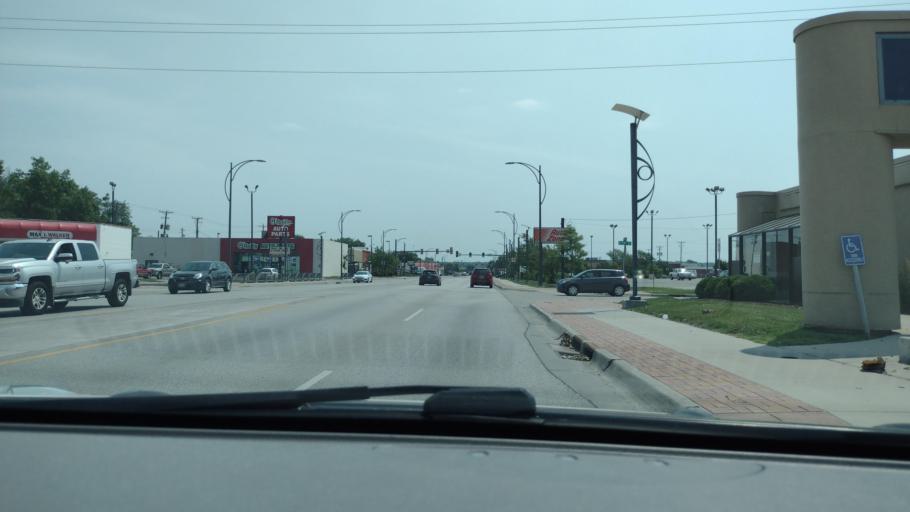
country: US
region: Iowa
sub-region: Pottawattamie County
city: Council Bluffs
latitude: 41.2619
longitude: -95.8911
